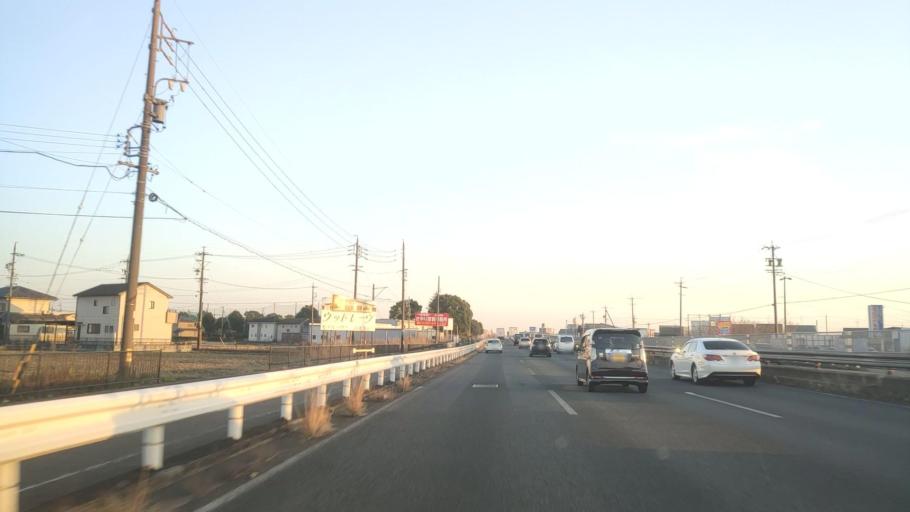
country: JP
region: Aichi
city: Kuroda
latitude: 35.3333
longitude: 136.8023
